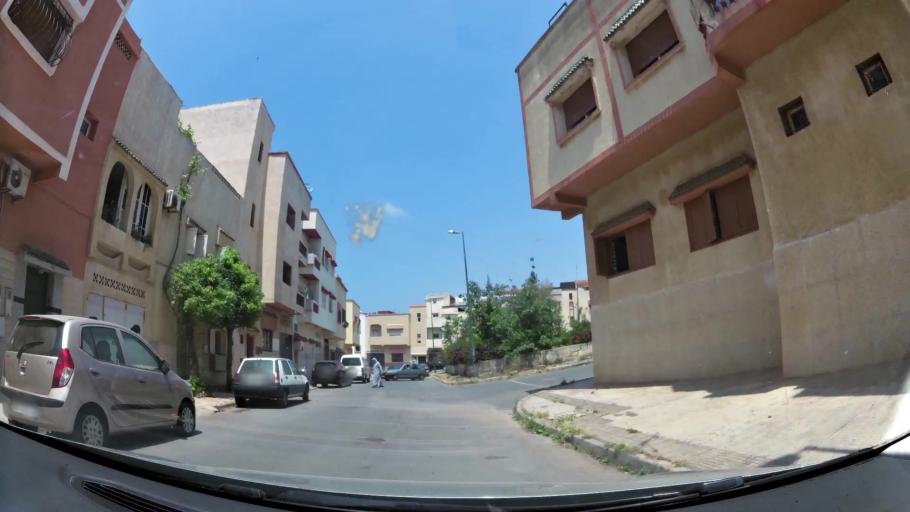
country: MA
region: Rabat-Sale-Zemmour-Zaer
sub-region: Skhirate-Temara
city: Temara
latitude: 33.9763
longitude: -6.8956
